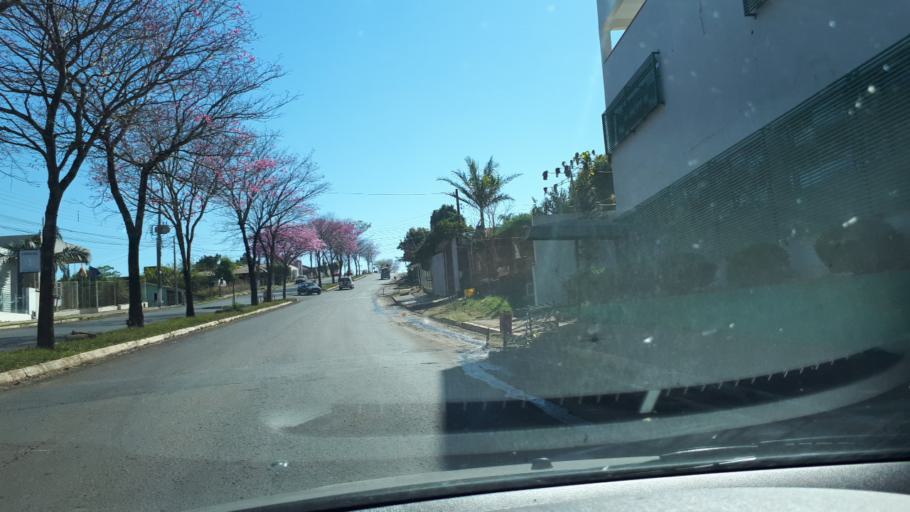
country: BR
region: Santa Catarina
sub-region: Chapeco
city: Chapeco
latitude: -27.1263
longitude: -52.6061
